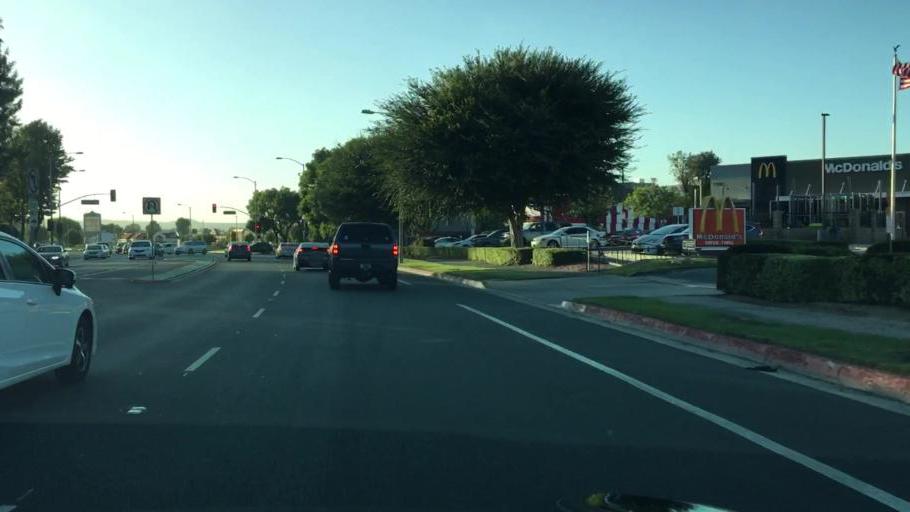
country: US
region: California
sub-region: Los Angeles County
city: Rowland Heights
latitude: 33.9896
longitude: -117.9122
